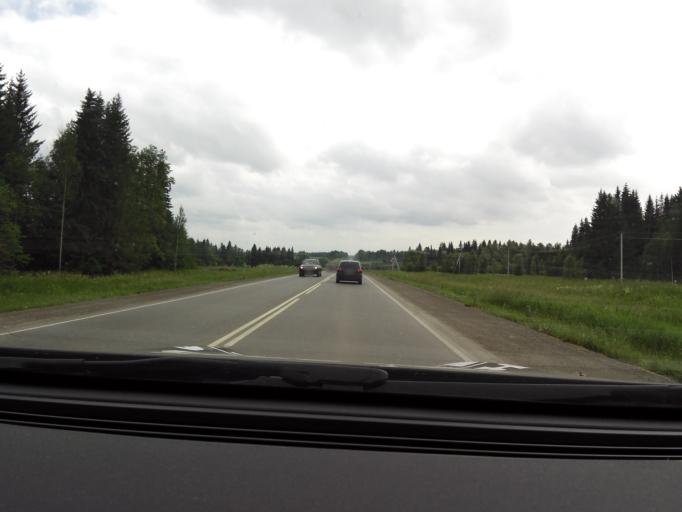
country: RU
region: Perm
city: Kukushtan
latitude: 57.6298
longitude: 56.4660
